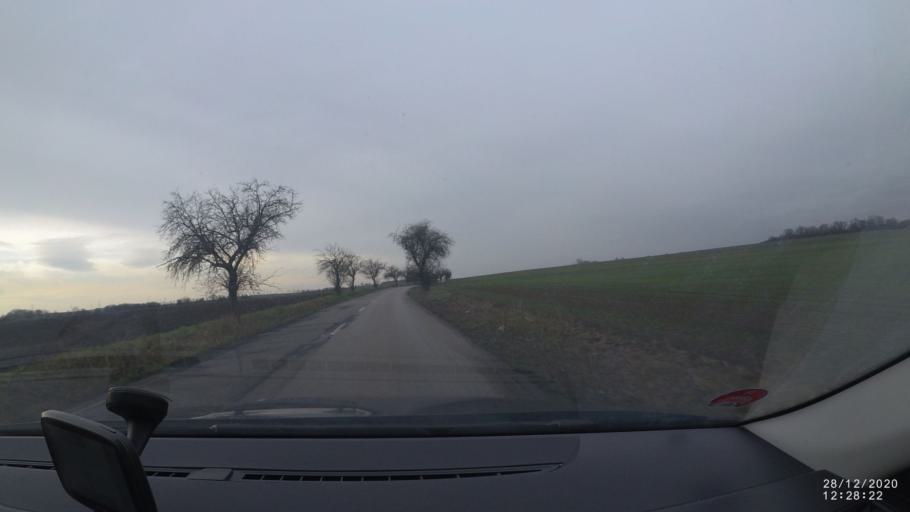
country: CZ
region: Central Bohemia
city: Brandys nad Labem-Stara Boleslav
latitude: 50.1952
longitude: 14.6322
